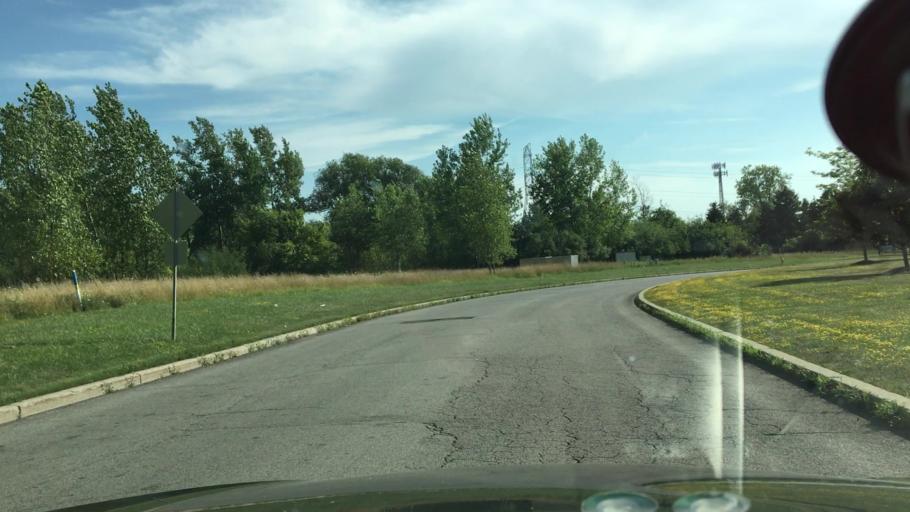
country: US
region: New York
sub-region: Erie County
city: Cheektowaga
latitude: 42.8480
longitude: -78.7422
